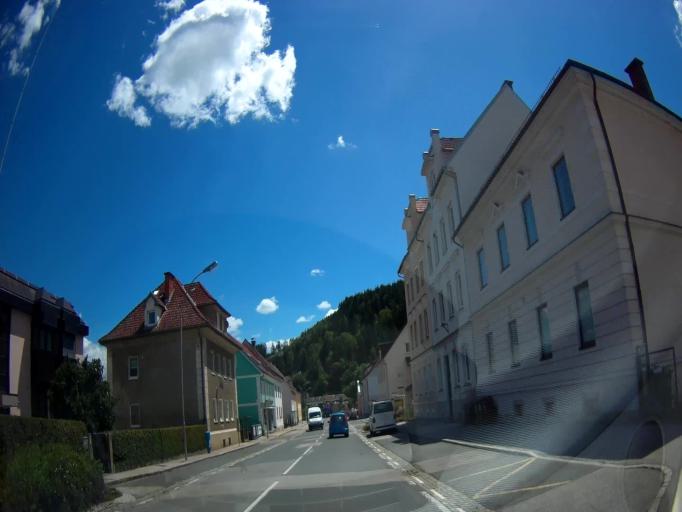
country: AT
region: Carinthia
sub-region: Politischer Bezirk Sankt Veit an der Glan
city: Sankt Veit an der Glan
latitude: 46.7625
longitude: 14.3643
